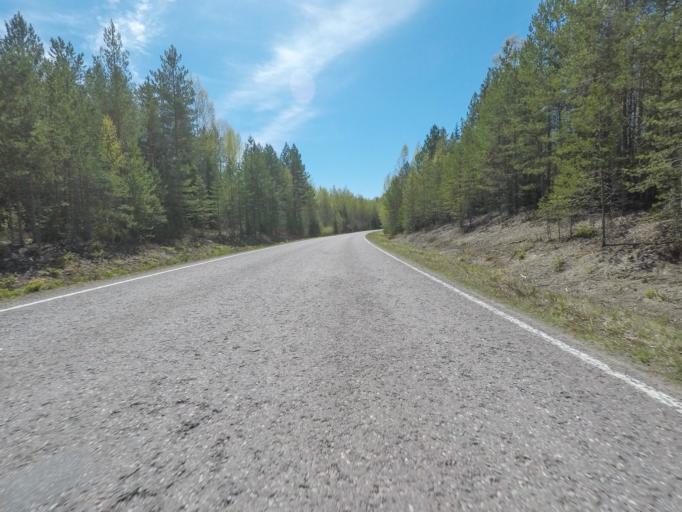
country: FI
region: Uusimaa
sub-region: Helsinki
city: Kaerkoelae
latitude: 60.5923
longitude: 23.7996
